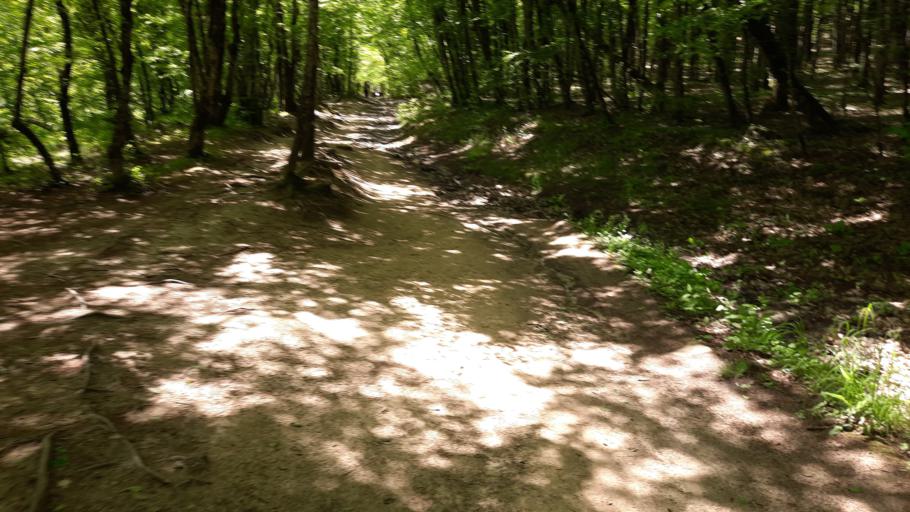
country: RU
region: Krasnodarskiy
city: Divnomorskoye
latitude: 44.5560
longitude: 38.2519
